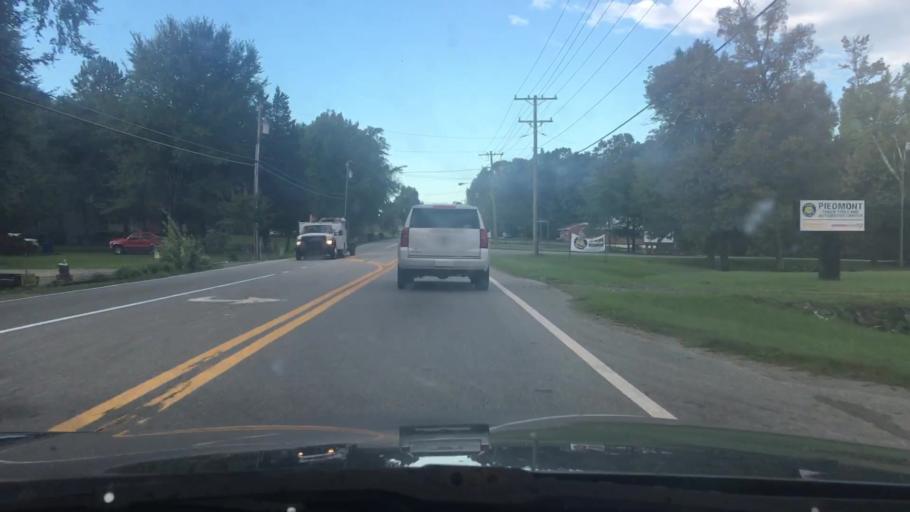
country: US
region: North Carolina
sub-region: Alamance County
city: Green Level
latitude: 36.1272
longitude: -79.3470
